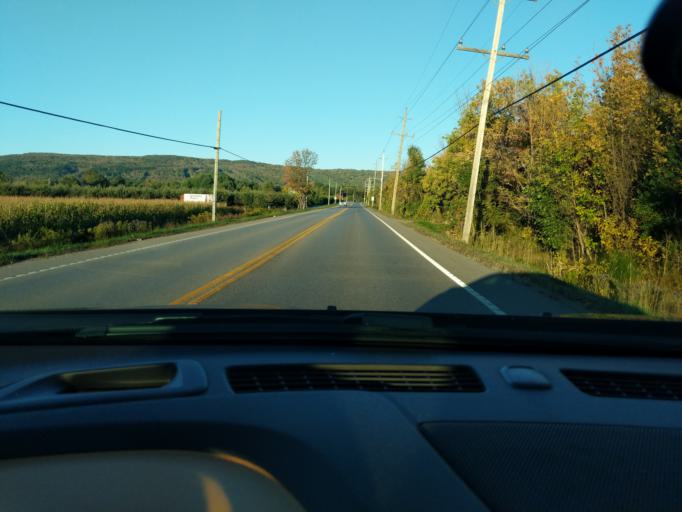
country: CA
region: Ontario
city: Collingwood
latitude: 44.4985
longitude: -80.2699
